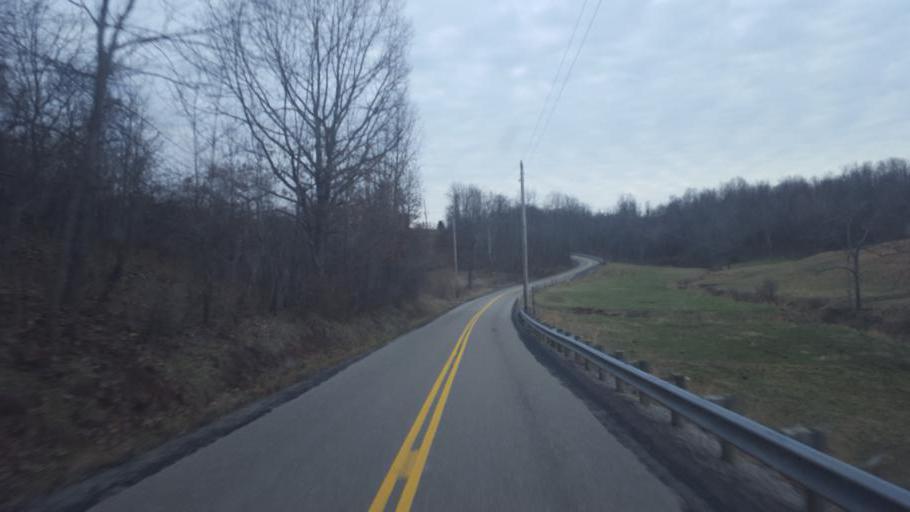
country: US
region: Ohio
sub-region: Gallia County
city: Gallipolis
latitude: 38.7140
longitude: -82.3440
